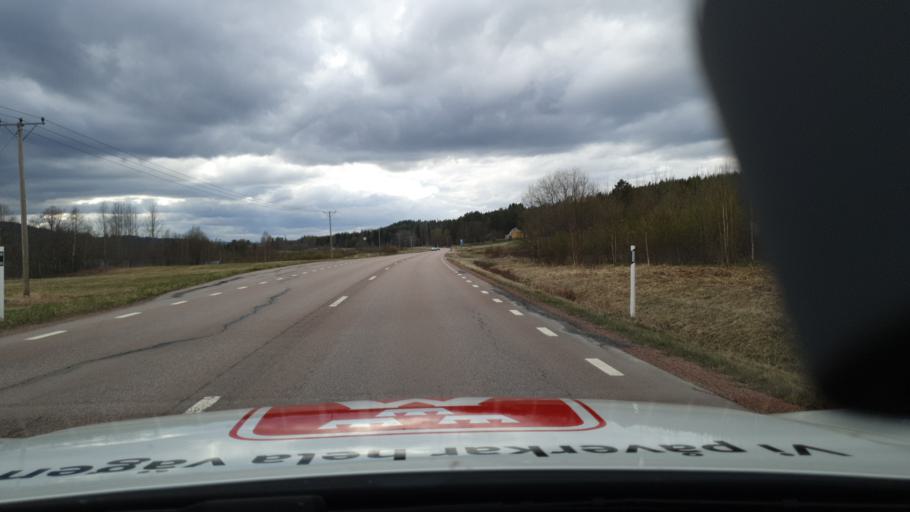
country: SE
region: Jaemtland
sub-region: Braecke Kommun
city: Braecke
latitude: 63.1584
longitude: 15.7528
